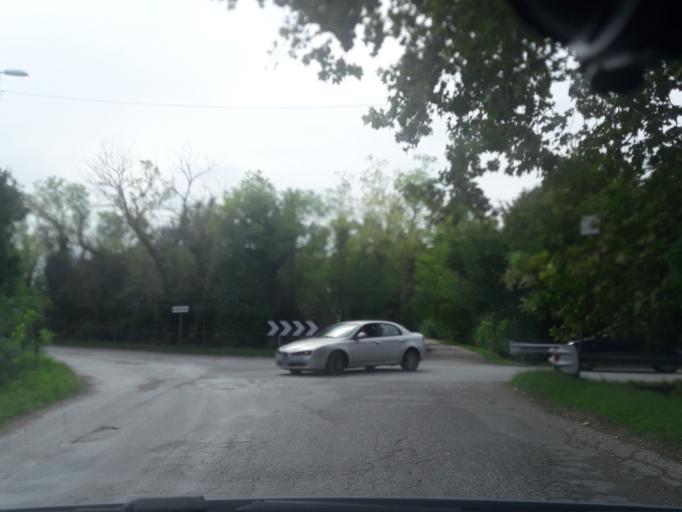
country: IT
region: Friuli Venezia Giulia
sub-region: Provincia di Udine
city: Pradamano
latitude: 46.0619
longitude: 13.2832
